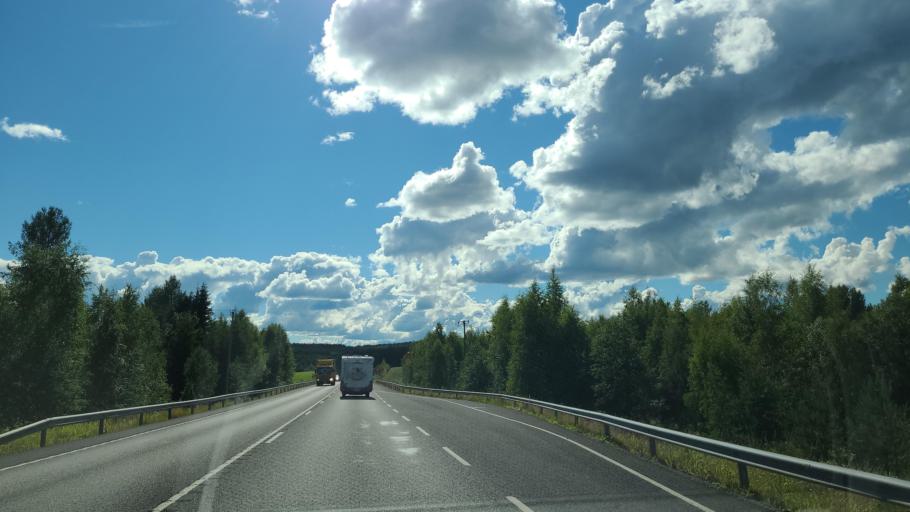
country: FI
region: Central Finland
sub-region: Jaemsae
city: Jaemsae
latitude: 61.8360
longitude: 25.1137
